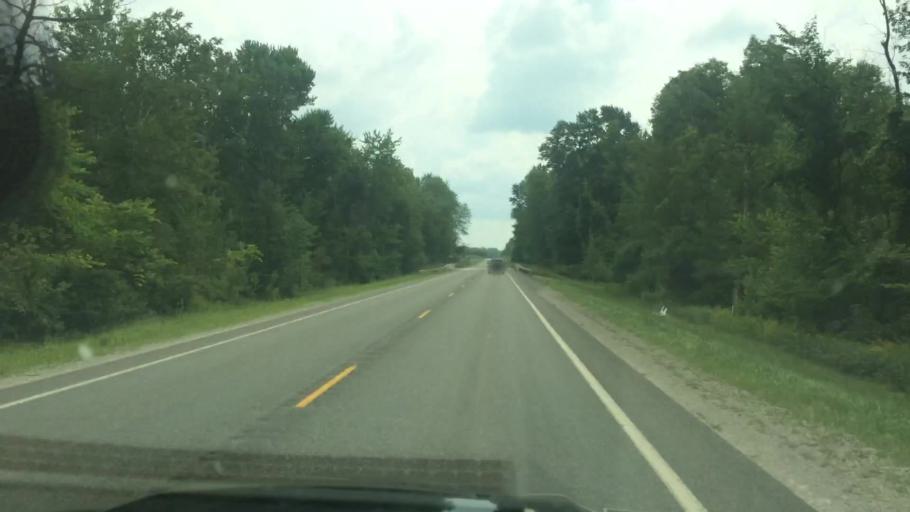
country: US
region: Michigan
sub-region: Tuscola County
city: Cass City
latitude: 43.6415
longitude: -83.0979
